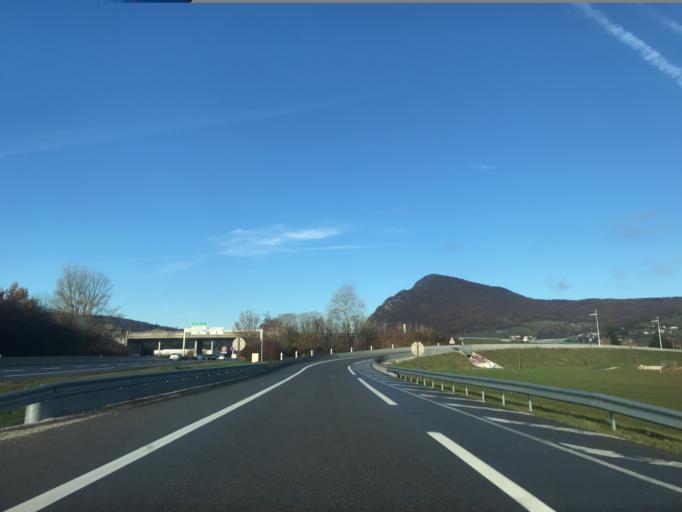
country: FR
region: Rhone-Alpes
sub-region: Departement de la Haute-Savoie
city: Epagny
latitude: 45.9308
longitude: 6.0867
